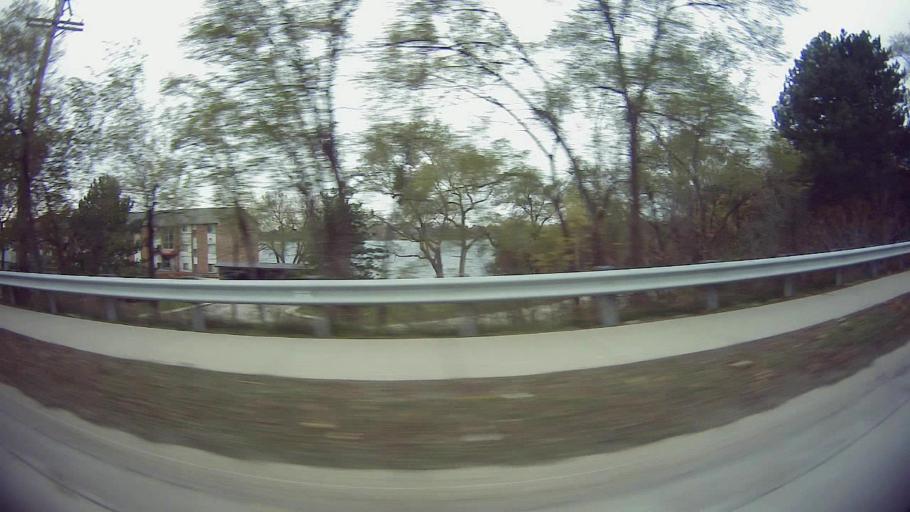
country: US
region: Michigan
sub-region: Oakland County
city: Sylvan Lake
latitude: 42.6131
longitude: -83.3082
